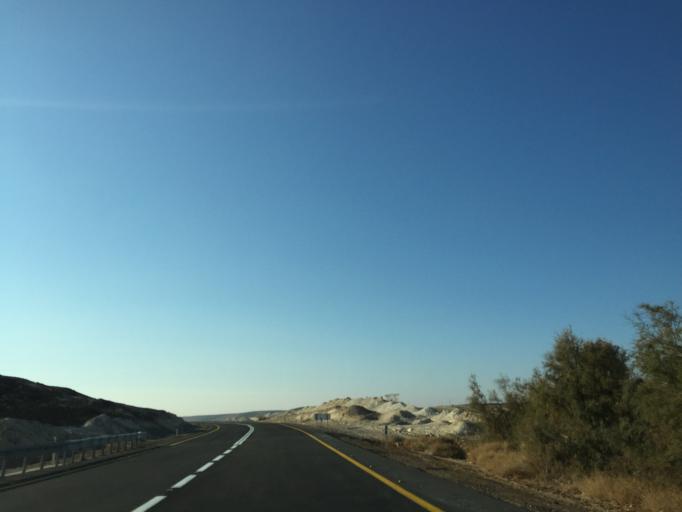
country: IL
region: Southern District
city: Mitzpe Ramon
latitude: 30.2534
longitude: 35.0235
